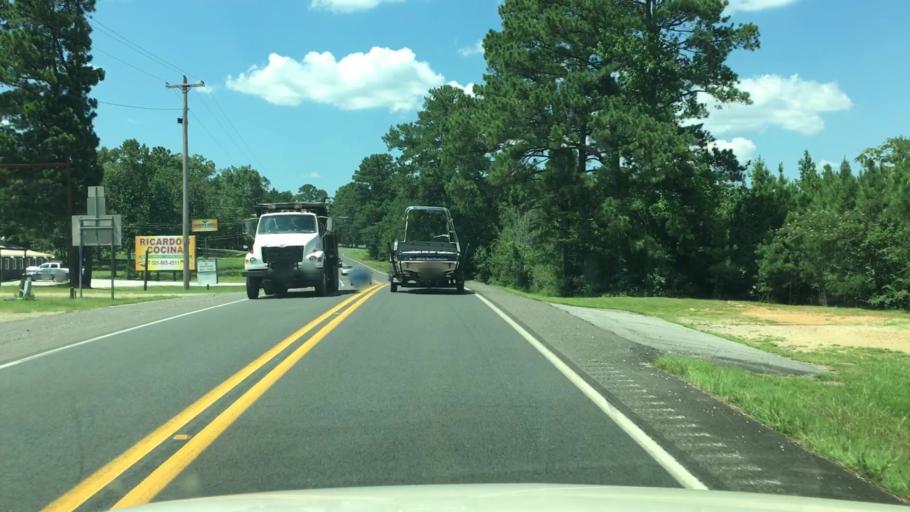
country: US
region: Arkansas
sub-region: Garland County
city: Lake Hamilton
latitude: 34.3185
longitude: -93.1717
